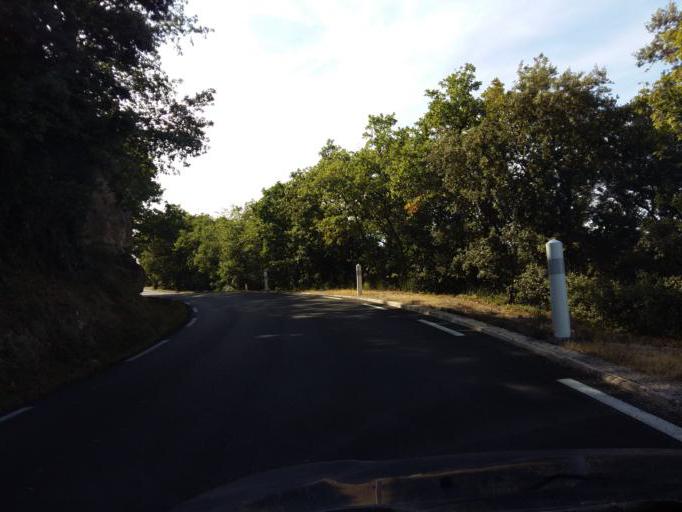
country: FR
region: Provence-Alpes-Cote d'Azur
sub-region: Departement du Vaucluse
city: Venasque
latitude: 44.0105
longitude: 5.1351
